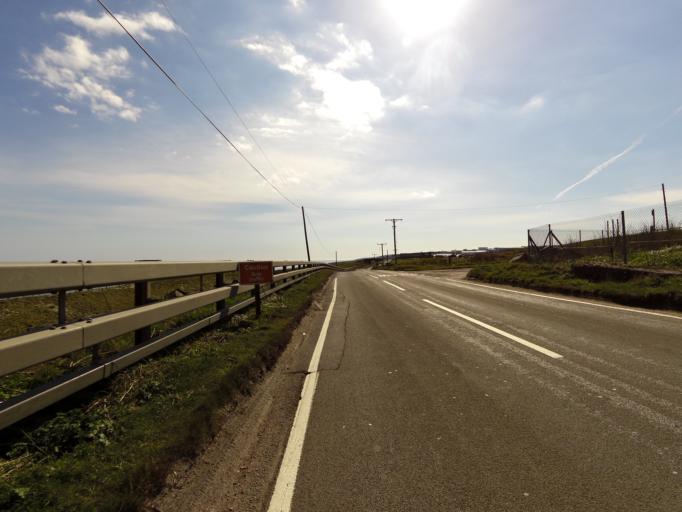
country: GB
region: Scotland
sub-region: Aberdeen City
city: Aberdeen
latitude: 57.1249
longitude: -2.0551
